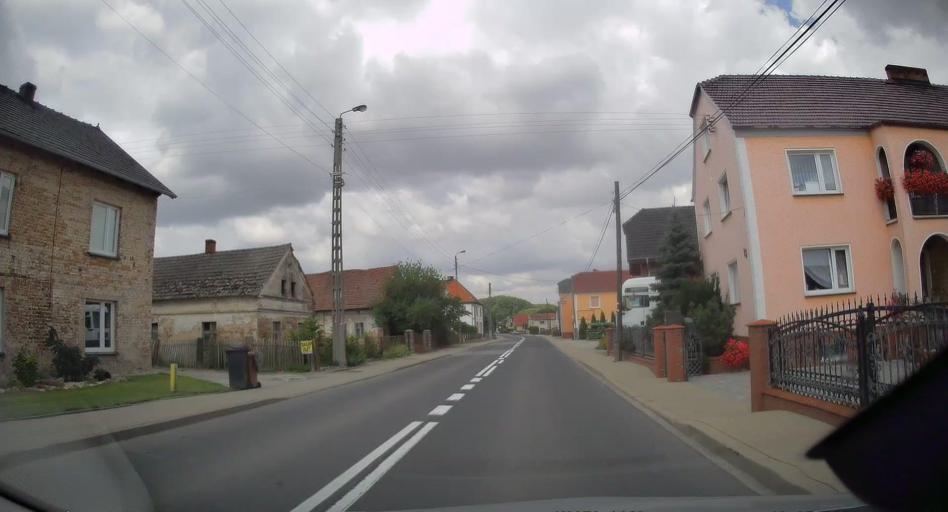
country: PL
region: Opole Voivodeship
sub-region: Powiat prudnicki
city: Twardawa
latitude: 50.3364
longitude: 17.9662
